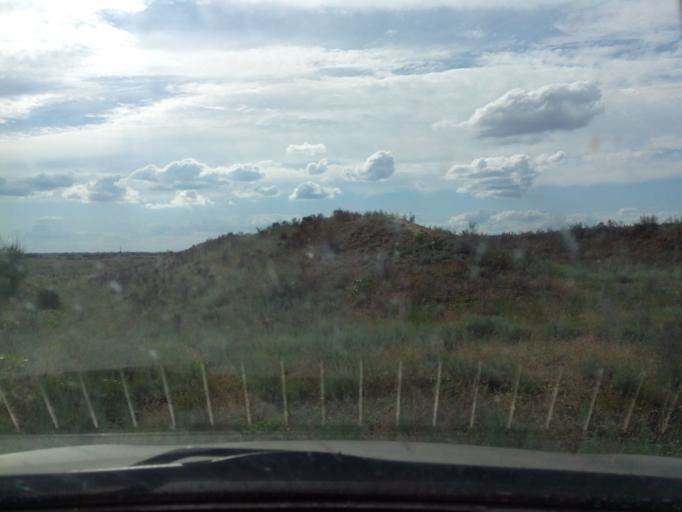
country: RU
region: Volgograd
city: Leninsk
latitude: 48.6811
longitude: 45.3673
